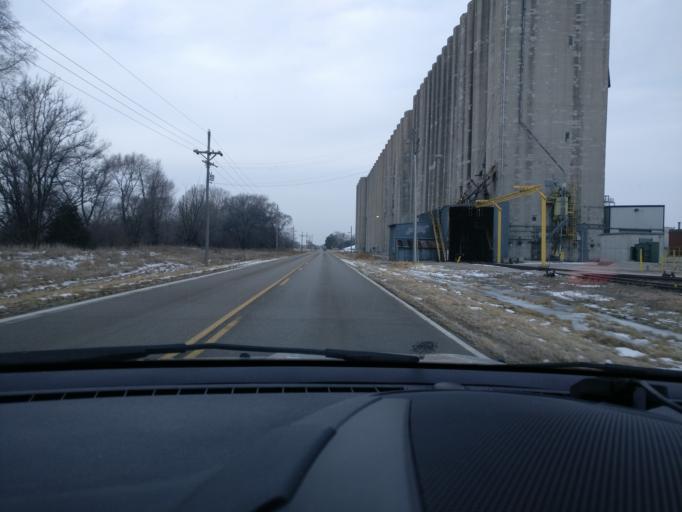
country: US
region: Nebraska
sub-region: Dodge County
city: Fremont
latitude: 41.4473
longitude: -96.5532
